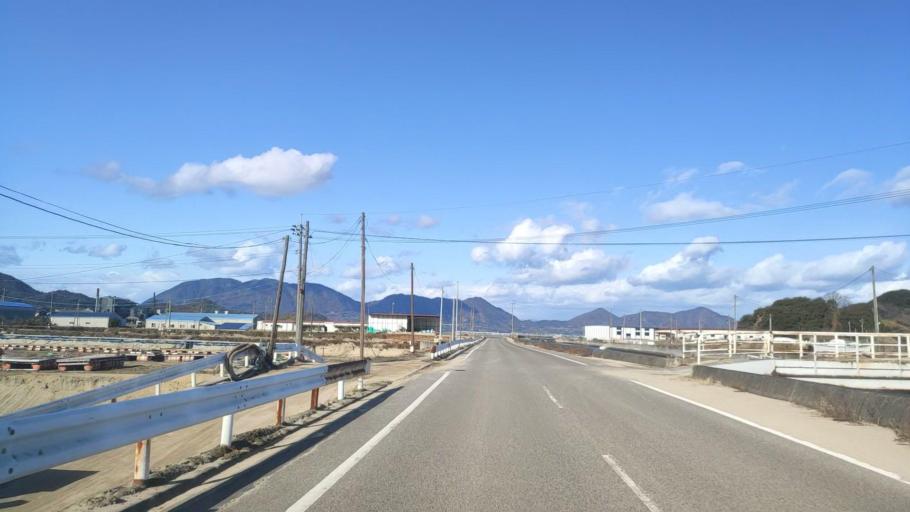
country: JP
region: Hiroshima
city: Innoshima
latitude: 34.2136
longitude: 133.1219
